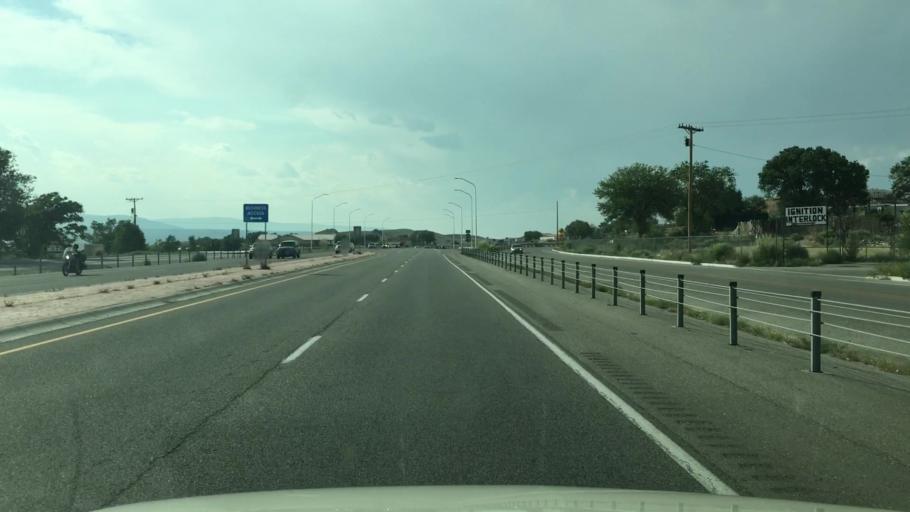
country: US
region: New Mexico
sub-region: Santa Fe County
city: El Valle de Arroyo Seco
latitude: 35.9675
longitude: -106.0356
